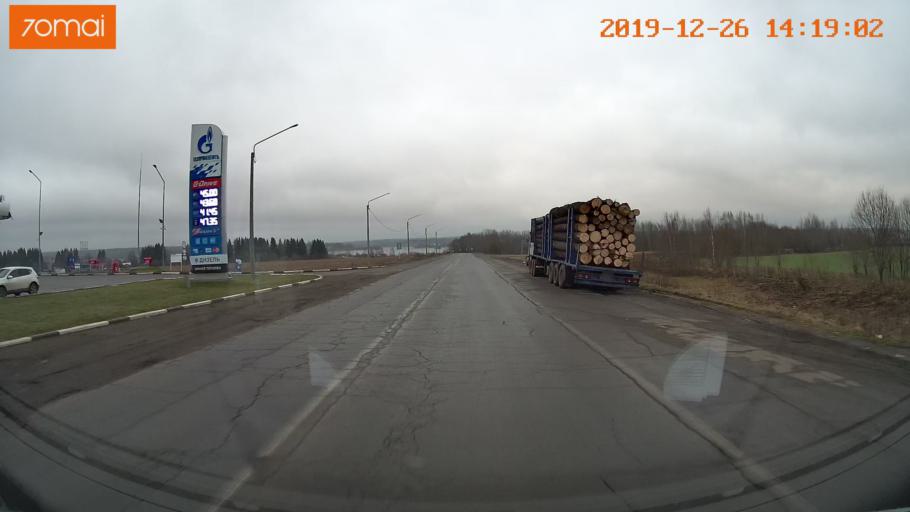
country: RU
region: Jaroslavl
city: Poshekhon'ye
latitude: 58.5122
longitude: 39.1076
